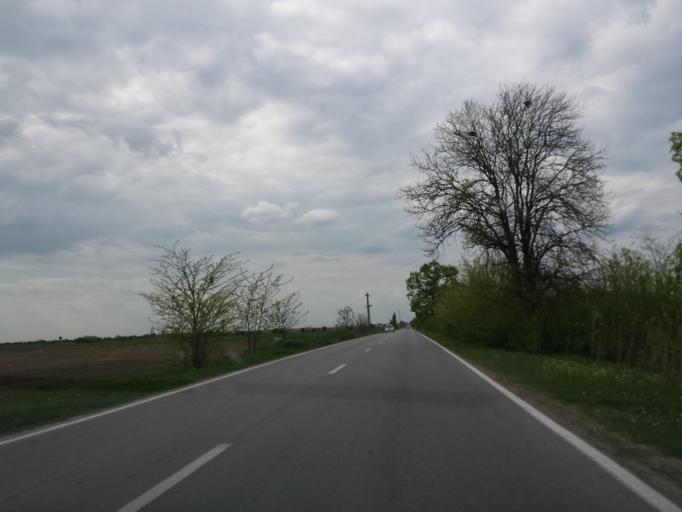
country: RO
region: Timis
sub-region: Comuna Sanpetru Mare
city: Sanpetru Mare
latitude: 46.0312
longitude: 20.6602
